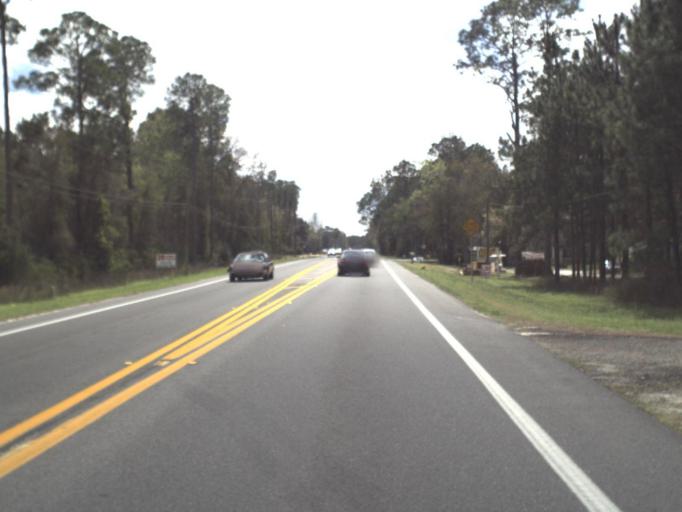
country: US
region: Florida
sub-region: Wakulla County
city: Crawfordville
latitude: 30.2269
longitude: -84.3624
